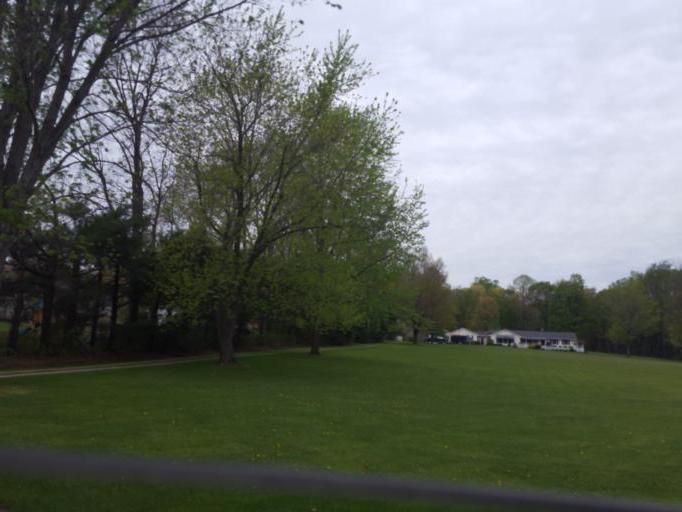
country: US
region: Ohio
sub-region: Richland County
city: Lexington
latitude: 40.7095
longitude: -82.6098
